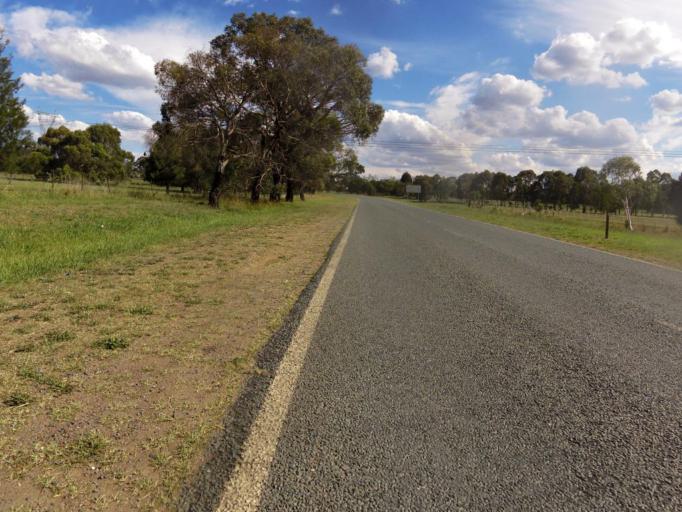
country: AU
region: Australian Capital Territory
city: Belconnen
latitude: -35.1737
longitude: 149.0713
